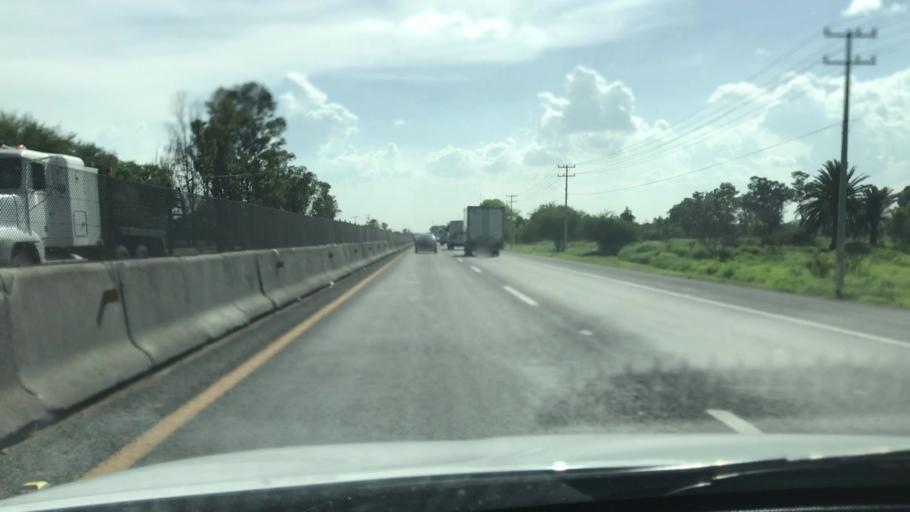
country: MX
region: Guanajuato
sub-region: Villagran
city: El Chinaco (El Pujido)
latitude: 20.5143
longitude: -100.9109
